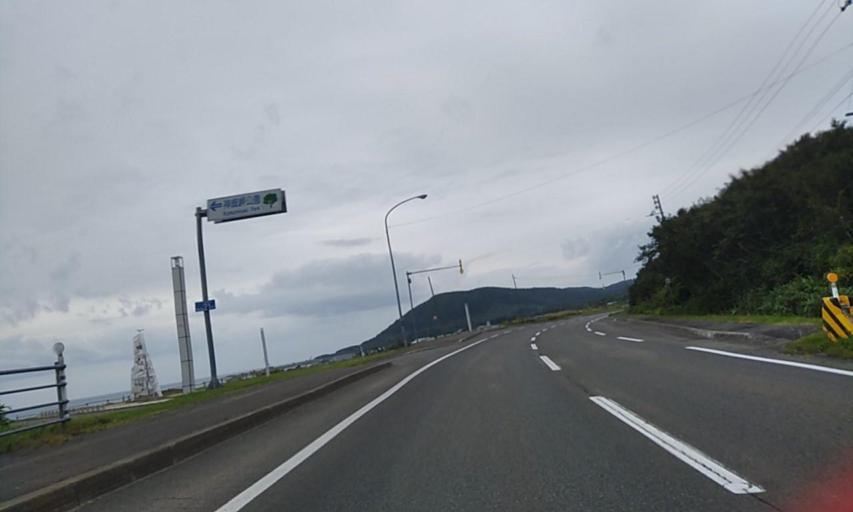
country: JP
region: Hokkaido
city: Nayoro
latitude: 45.0426
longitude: 142.5057
